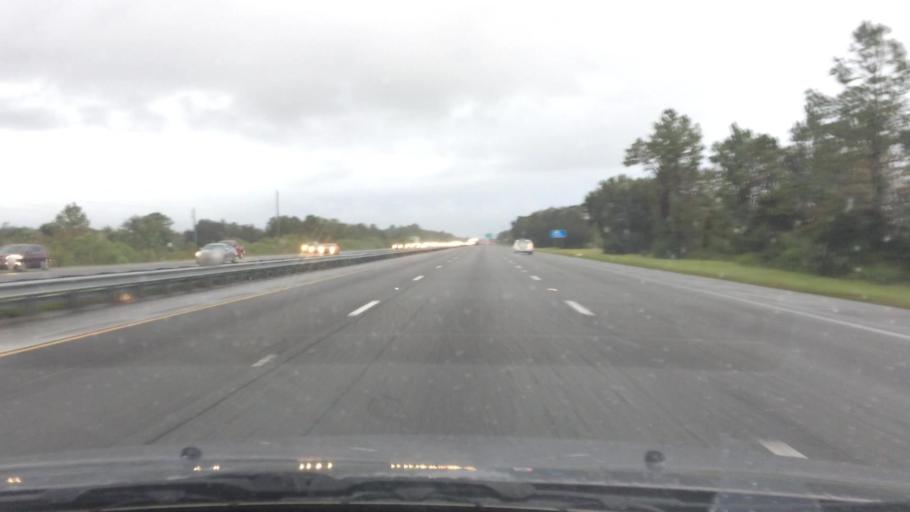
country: US
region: Florida
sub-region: Volusia County
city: Ormond-by-the-Sea
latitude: 29.3164
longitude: -81.1314
